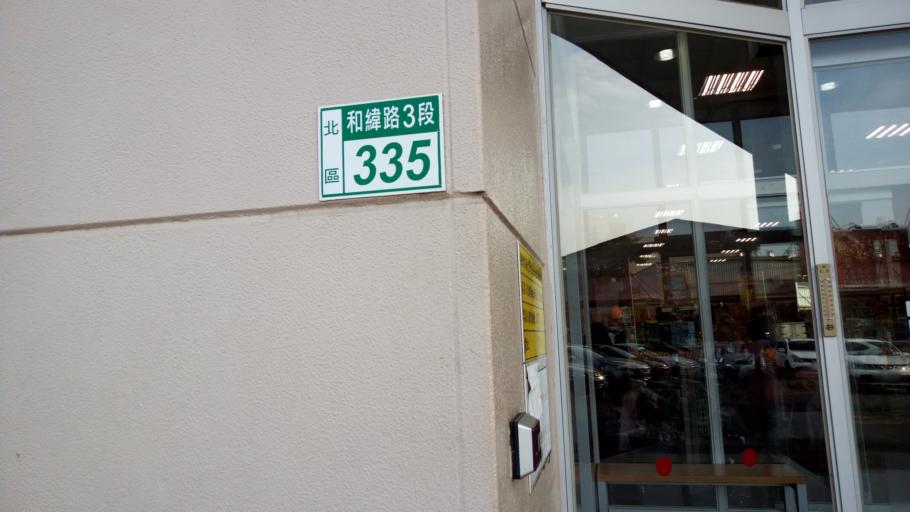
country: TW
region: Taiwan
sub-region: Tainan
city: Tainan
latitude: 23.0097
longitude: 120.1958
